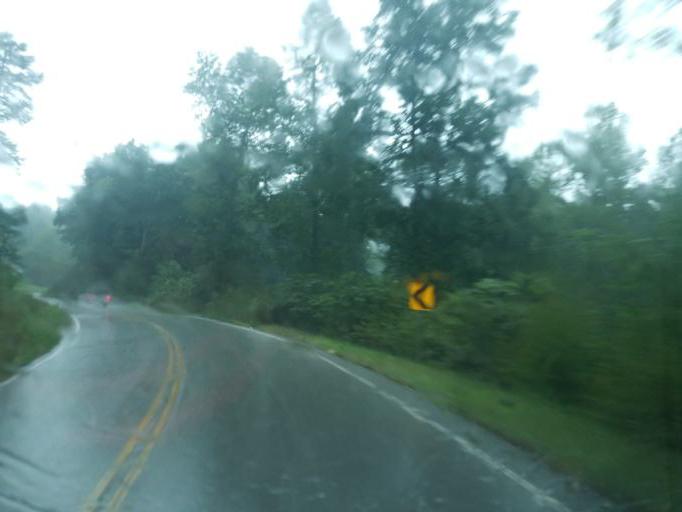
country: US
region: Kentucky
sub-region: Carter County
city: Olive Hill
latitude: 38.3414
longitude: -83.2005
